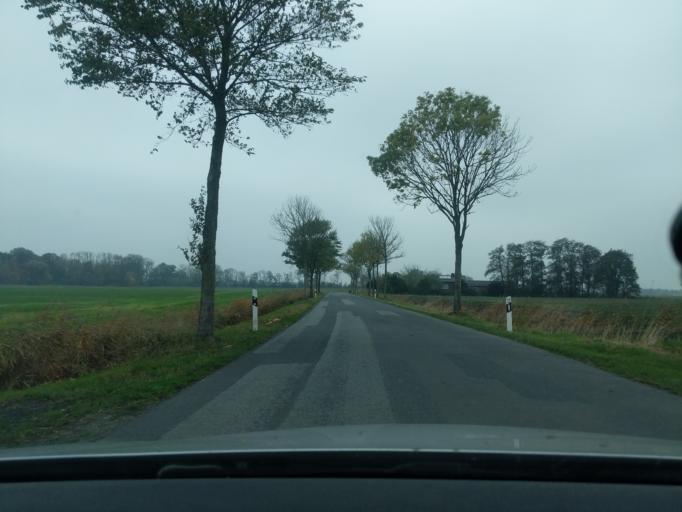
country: DE
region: Lower Saxony
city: Nordleda
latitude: 53.8244
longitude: 8.7987
